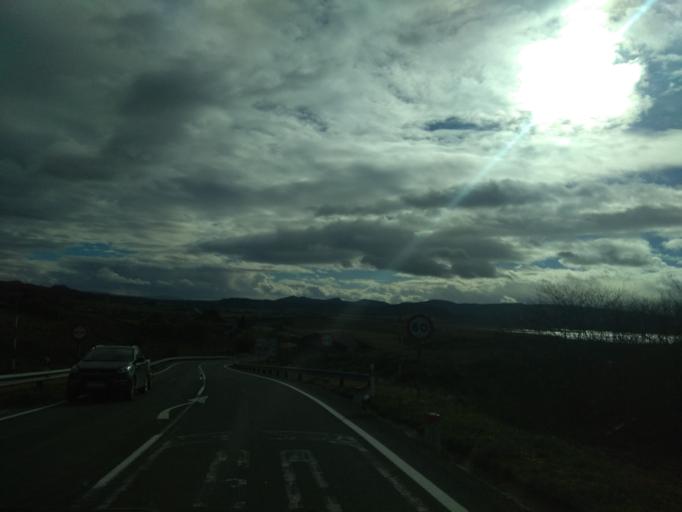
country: ES
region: Castille and Leon
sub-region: Provincia de Burgos
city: Arija
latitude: 43.0310
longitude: -3.8643
